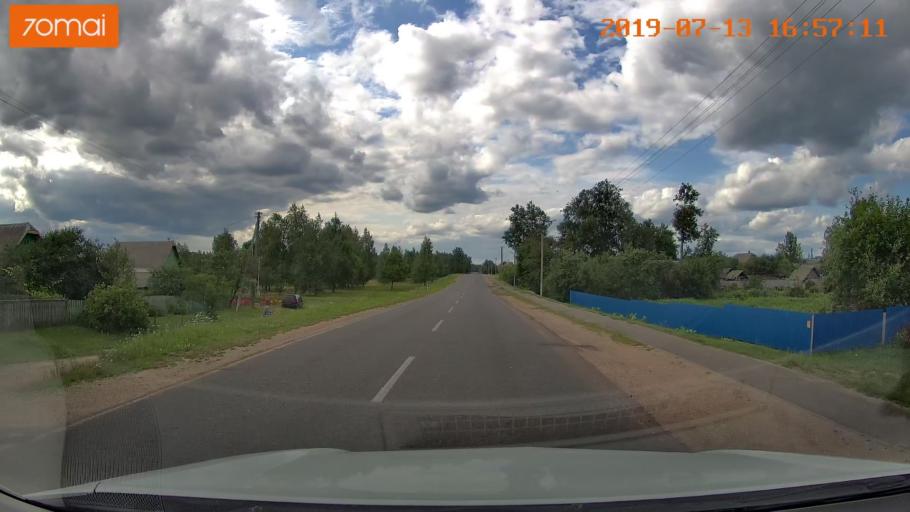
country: BY
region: Mogilev
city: Kirawsk
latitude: 53.2779
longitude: 29.4540
